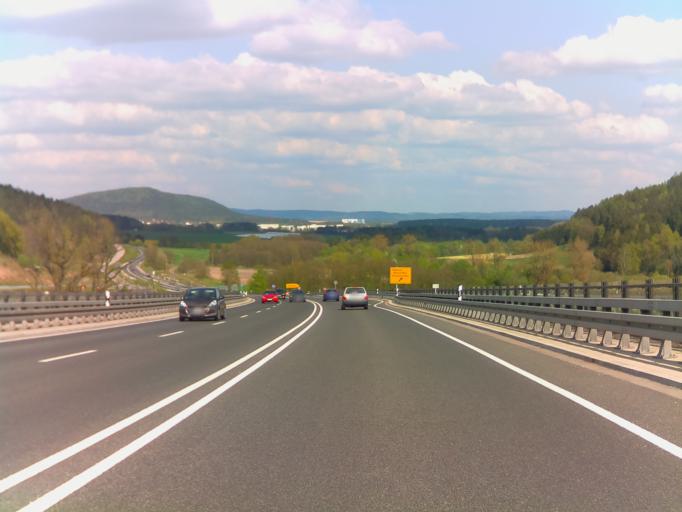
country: DE
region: Bavaria
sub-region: Upper Franconia
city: Rodental
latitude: 50.3055
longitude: 11.0578
